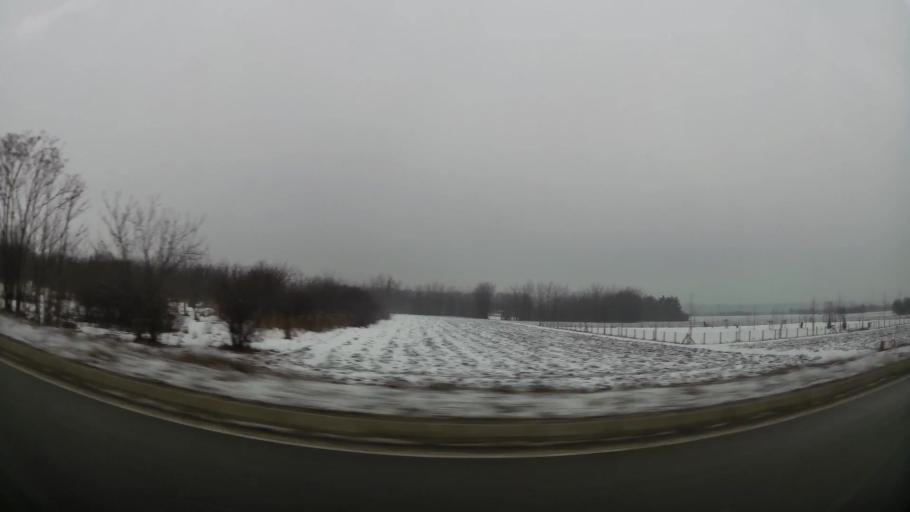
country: RS
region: Central Serbia
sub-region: Belgrade
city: Cukarica
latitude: 44.7628
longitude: 20.3890
